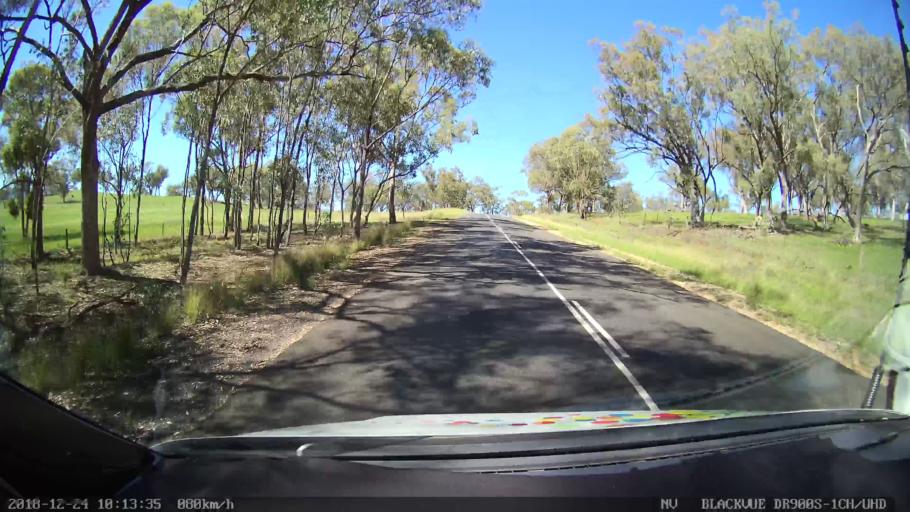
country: AU
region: New South Wales
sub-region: Liverpool Plains
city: Quirindi
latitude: -31.6914
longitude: 150.6387
